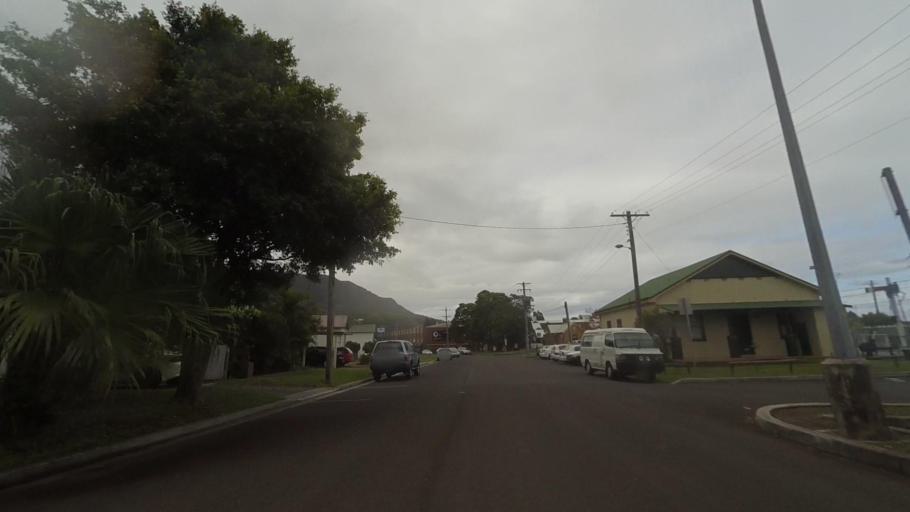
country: AU
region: New South Wales
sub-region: Wollongong
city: Bulli
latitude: -34.3188
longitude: 150.9179
